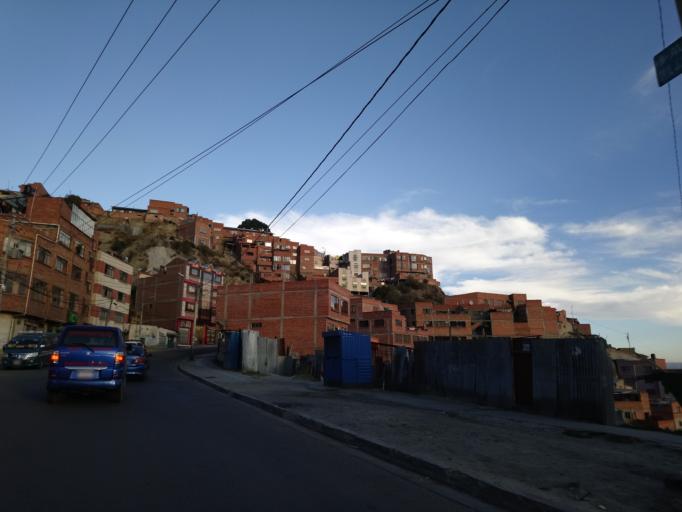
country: BO
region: La Paz
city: La Paz
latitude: -16.4850
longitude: -68.1368
